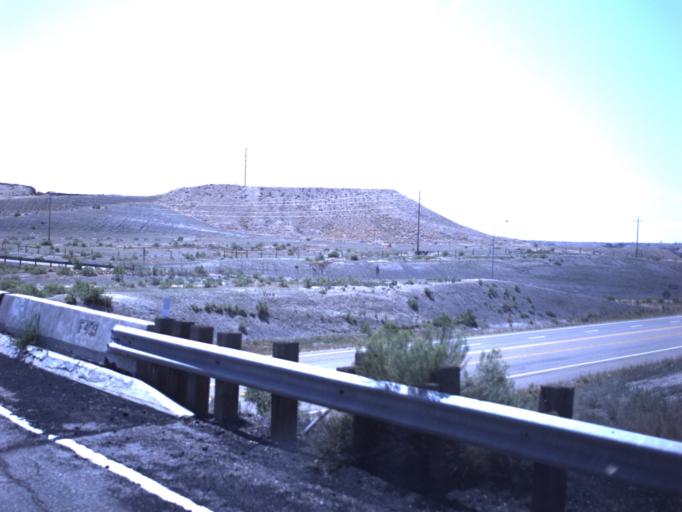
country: US
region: Utah
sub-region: Emery County
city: Castle Dale
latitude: 39.1766
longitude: -111.0472
